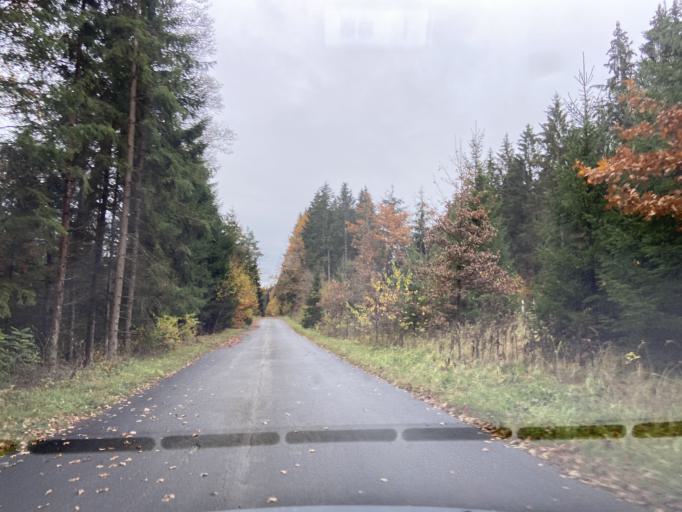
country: DE
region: Baden-Wuerttemberg
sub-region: Tuebingen Region
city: Krauchenwies
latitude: 48.0408
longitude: 9.2416
